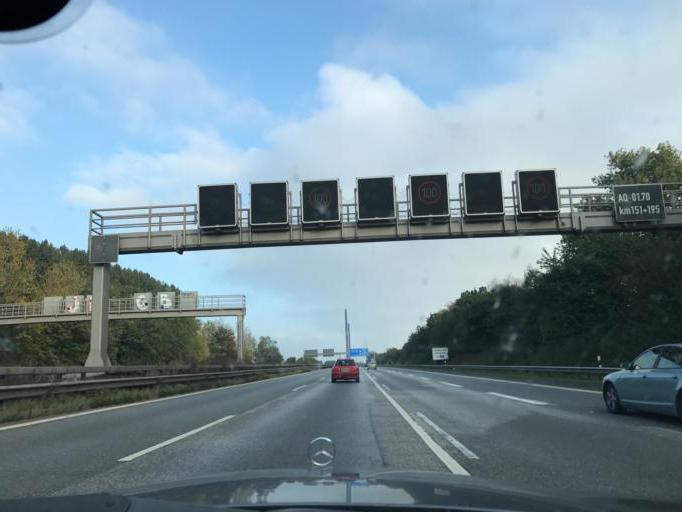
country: DE
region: Hamburg
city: Rothenburgsort
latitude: 53.5095
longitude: 10.0503
